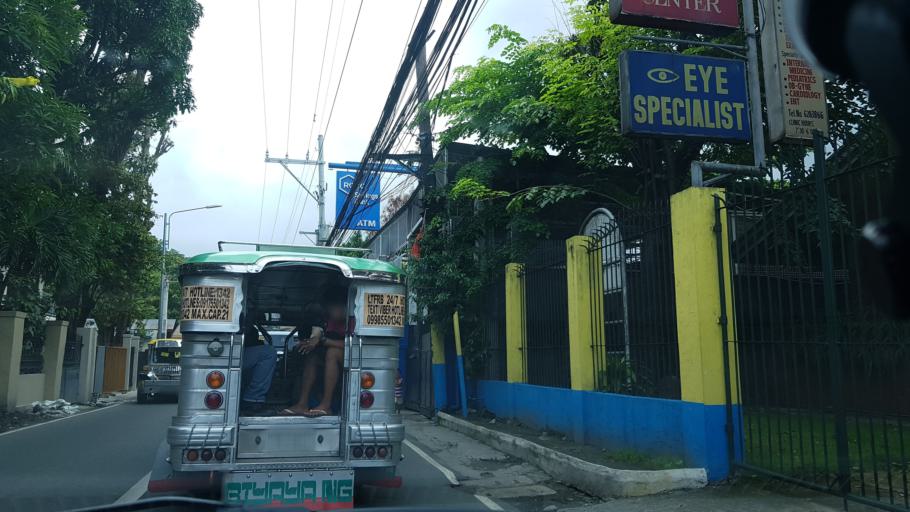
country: PH
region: Calabarzon
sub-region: Province of Rizal
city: Pateros
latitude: 14.5460
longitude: 121.0692
